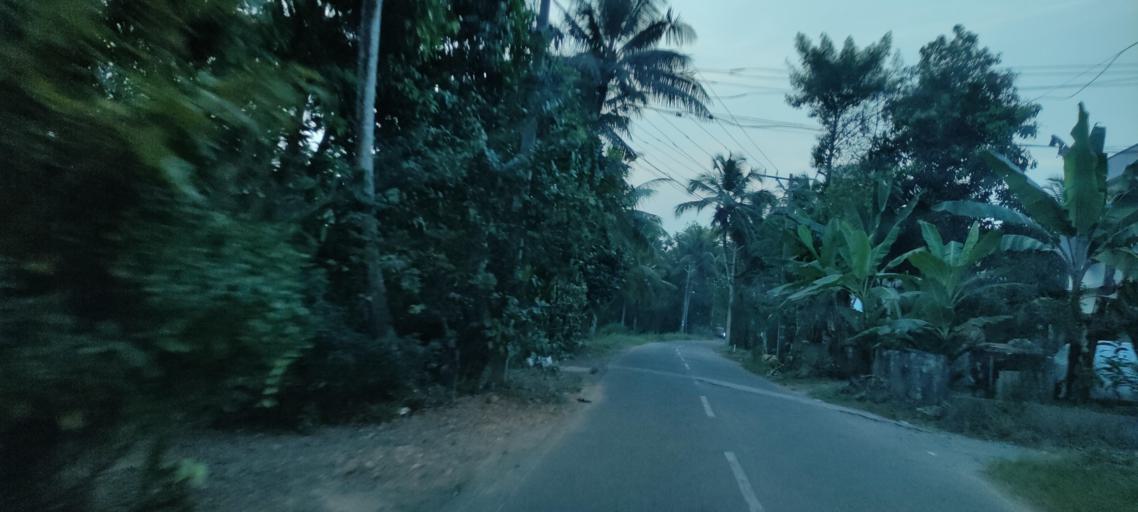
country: IN
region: Kerala
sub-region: Pattanamtitta
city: Tiruvalla
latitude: 9.3311
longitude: 76.5105
